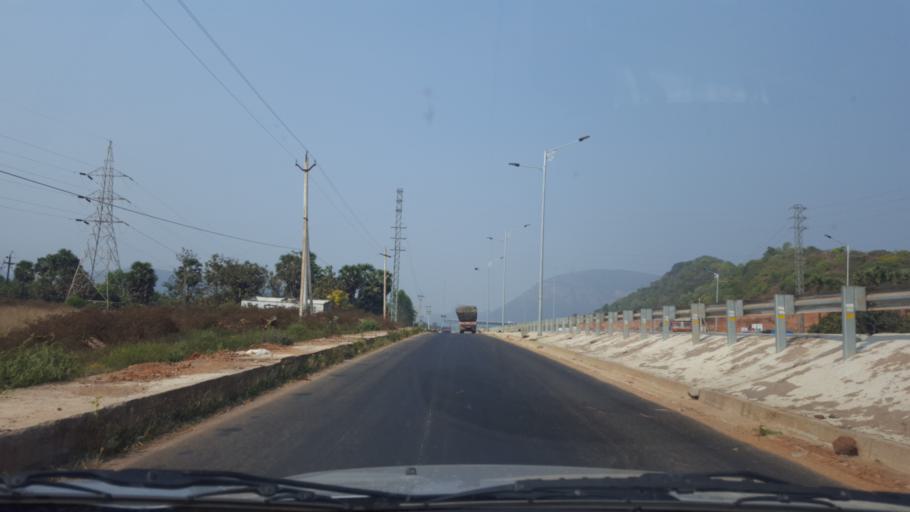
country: IN
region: Andhra Pradesh
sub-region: Vishakhapatnam
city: Bhimunipatnam
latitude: 17.8881
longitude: 83.3495
